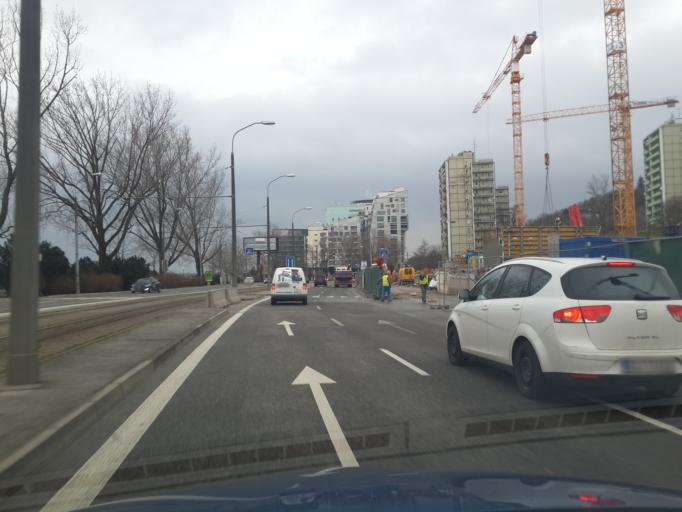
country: SK
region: Bratislavsky
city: Bratislava
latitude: 48.1403
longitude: 17.0959
